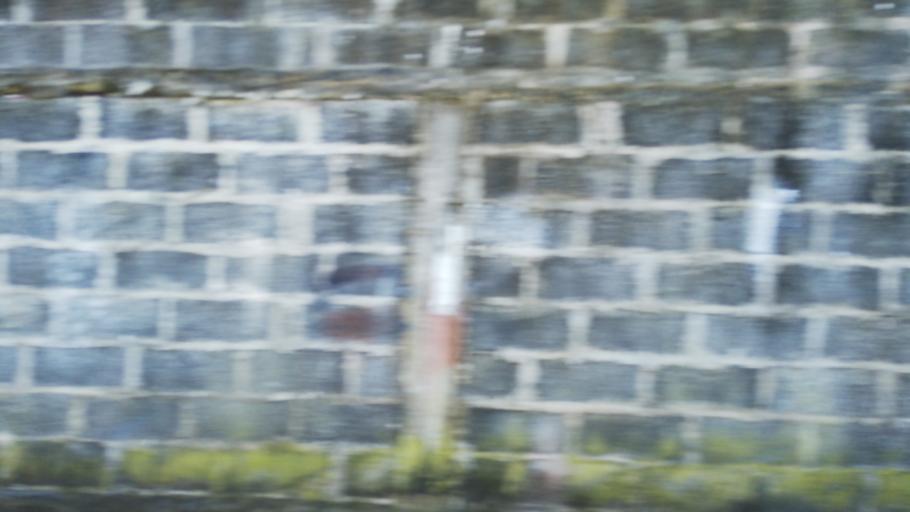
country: MU
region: Plaines Wilhems
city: Ebene
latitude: -20.2362
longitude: 57.4778
